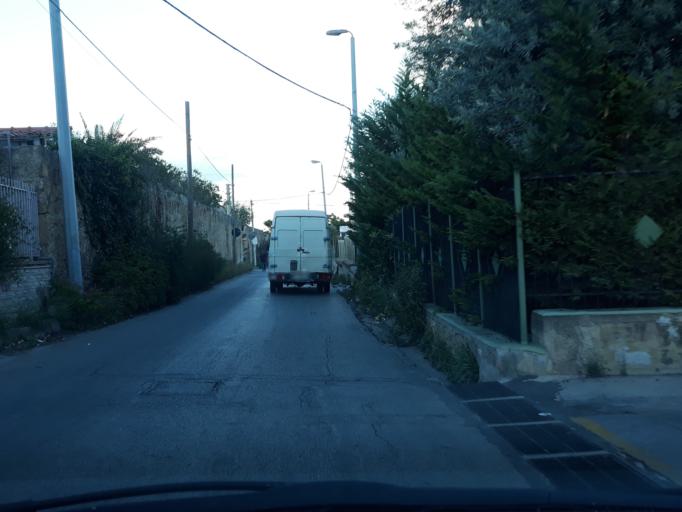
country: IT
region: Sicily
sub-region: Palermo
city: Villa Ciambra
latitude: 38.0765
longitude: 13.3109
